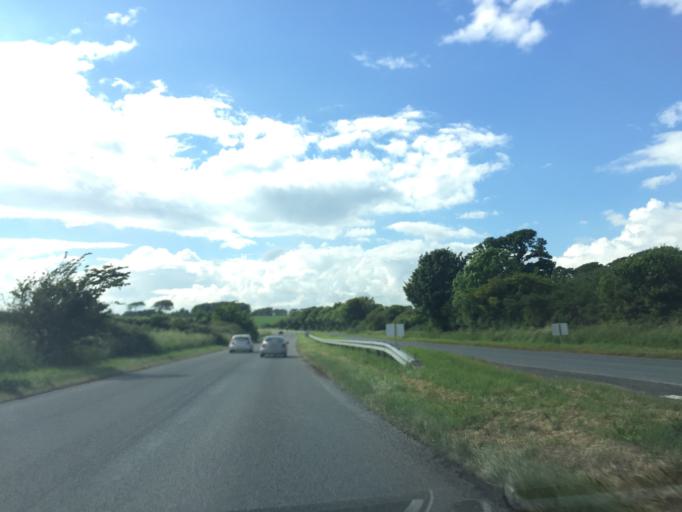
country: GB
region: England
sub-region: Dorset
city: Overcombe
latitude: 50.6656
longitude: -2.3454
